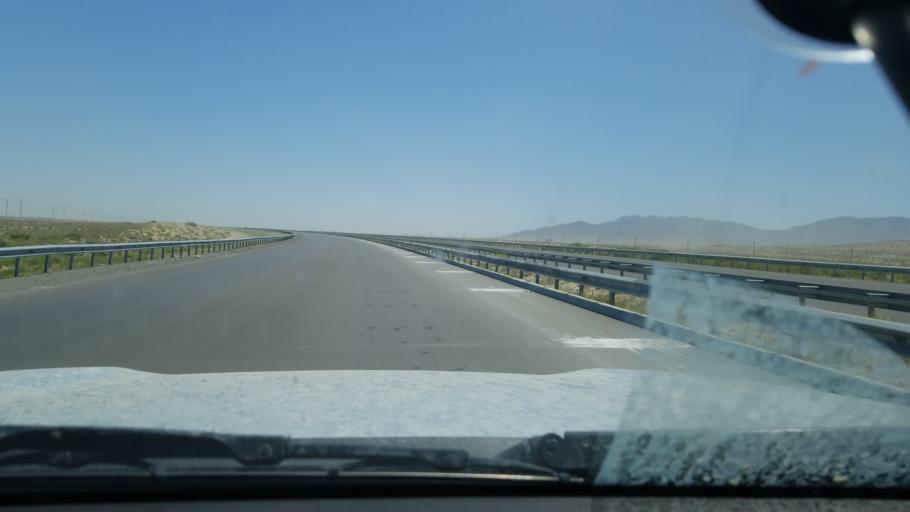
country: TM
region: Balkan
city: Gazanjyk
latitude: 39.2542
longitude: 55.3723
